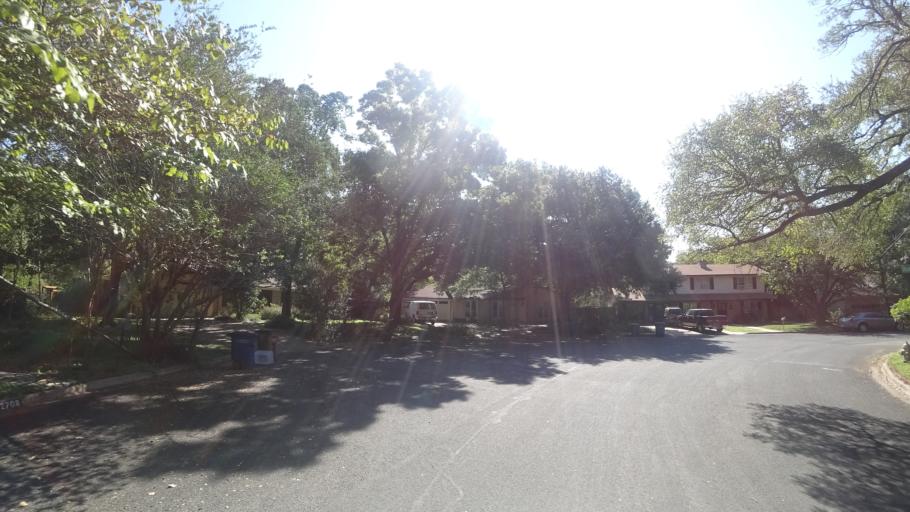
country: US
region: Texas
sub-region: Travis County
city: Austin
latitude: 30.3172
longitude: -97.6728
